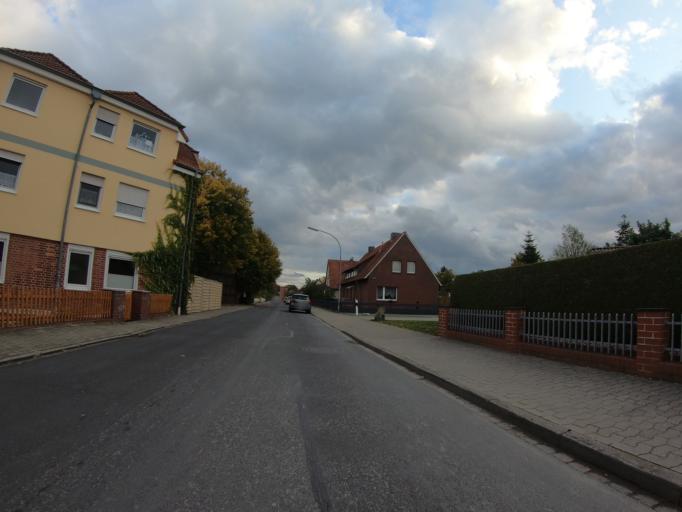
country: DE
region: Lower Saxony
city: Wagenhoff
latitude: 52.5168
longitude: 10.5322
